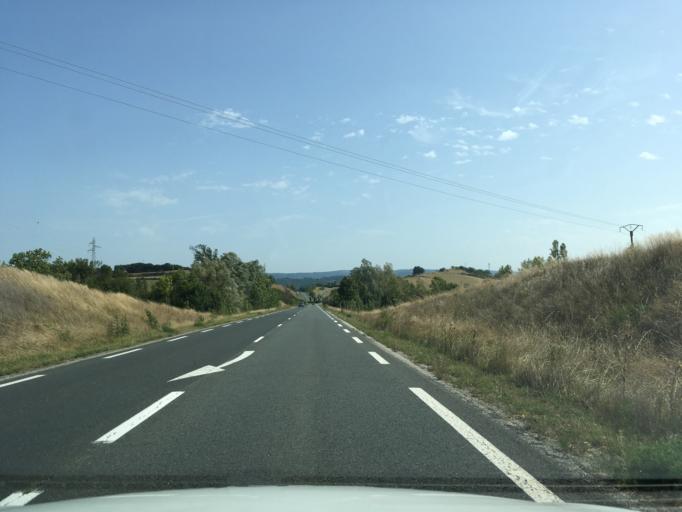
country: FR
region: Midi-Pyrenees
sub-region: Departement du Tarn
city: Lagarrigue
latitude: 43.5762
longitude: 2.2618
